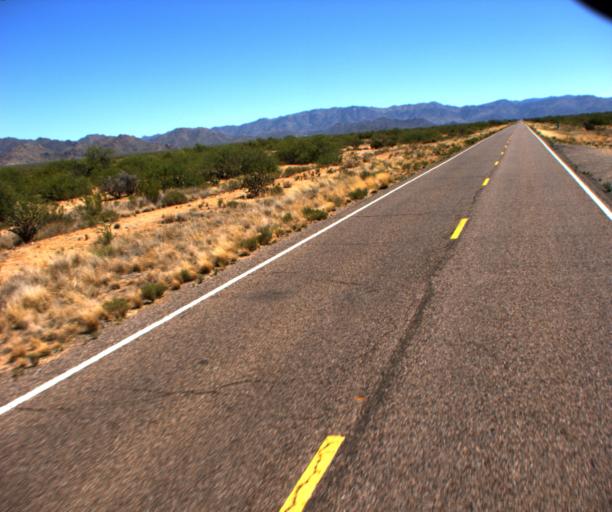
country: US
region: Arizona
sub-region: Yavapai County
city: Congress
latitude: 34.1298
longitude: -112.9345
